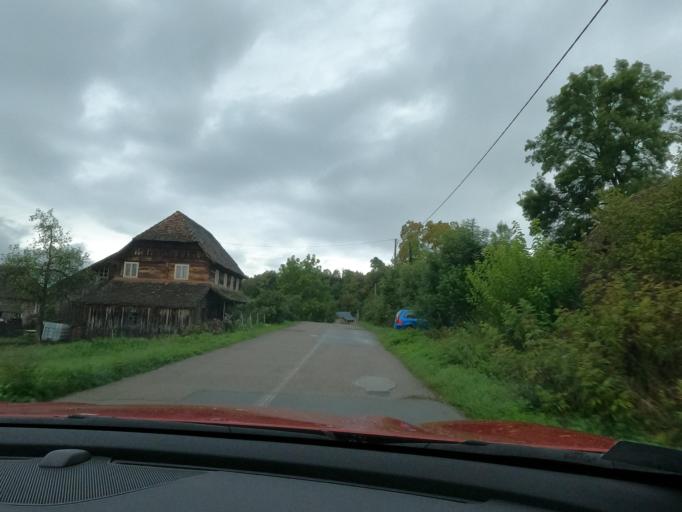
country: HR
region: Sisacko-Moslavacka
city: Glina
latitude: 45.2958
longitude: 16.1501
